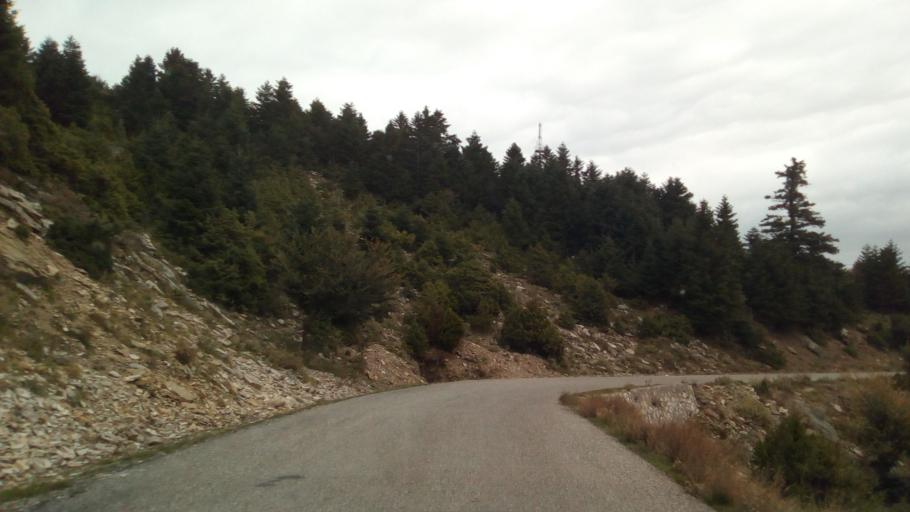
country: GR
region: West Greece
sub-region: Nomos Aitolias kai Akarnanias
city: Thermo
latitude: 38.6255
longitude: 21.8238
